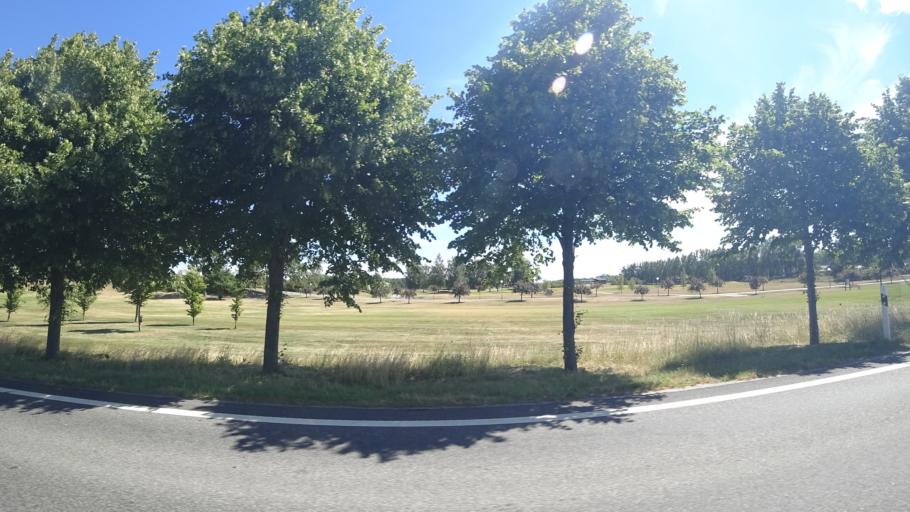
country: SE
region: Skane
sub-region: Kristianstads Kommun
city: Onnestad
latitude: 56.0637
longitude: 14.0841
